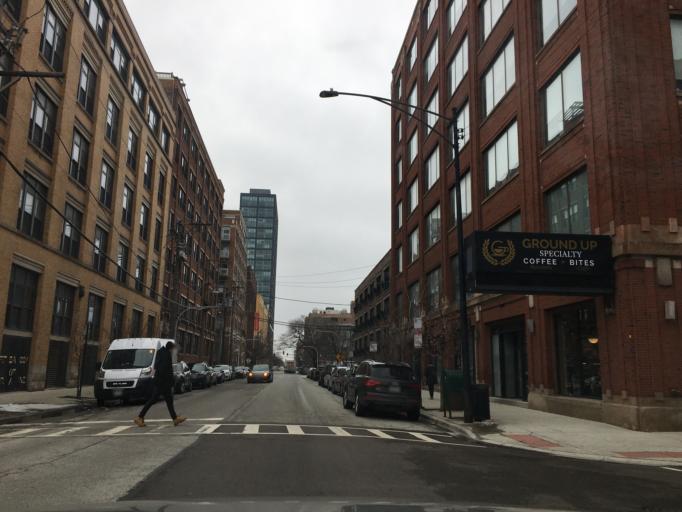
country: US
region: Illinois
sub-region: Cook County
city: Chicago
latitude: 41.8766
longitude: -87.6496
